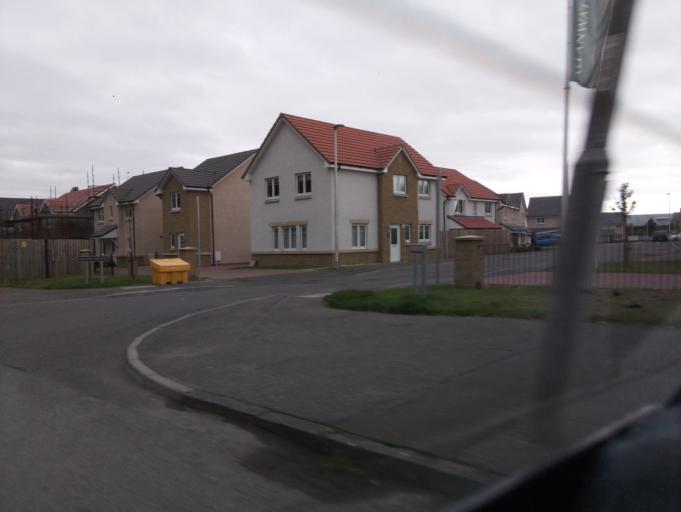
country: GB
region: Scotland
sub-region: Clackmannanshire
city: Alva
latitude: 56.1528
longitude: -3.7920
